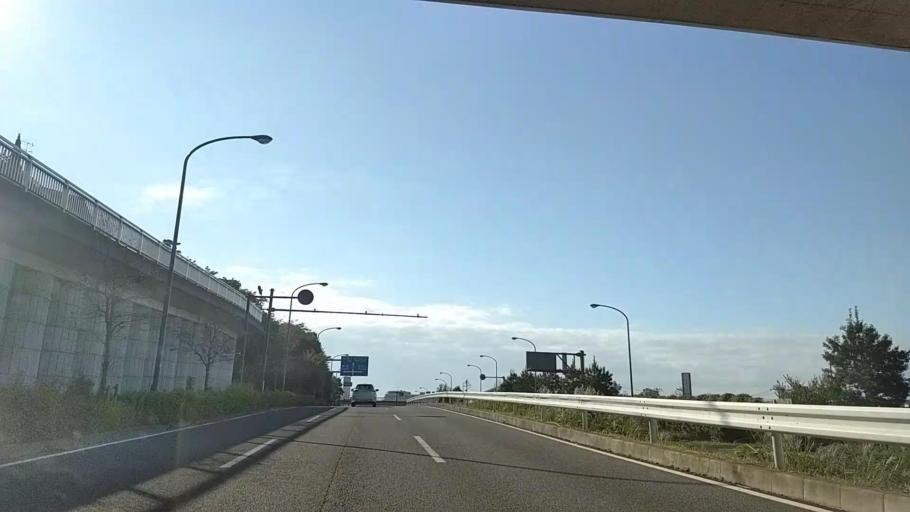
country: JP
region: Kanagawa
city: Yokohama
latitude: 35.4592
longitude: 139.5629
